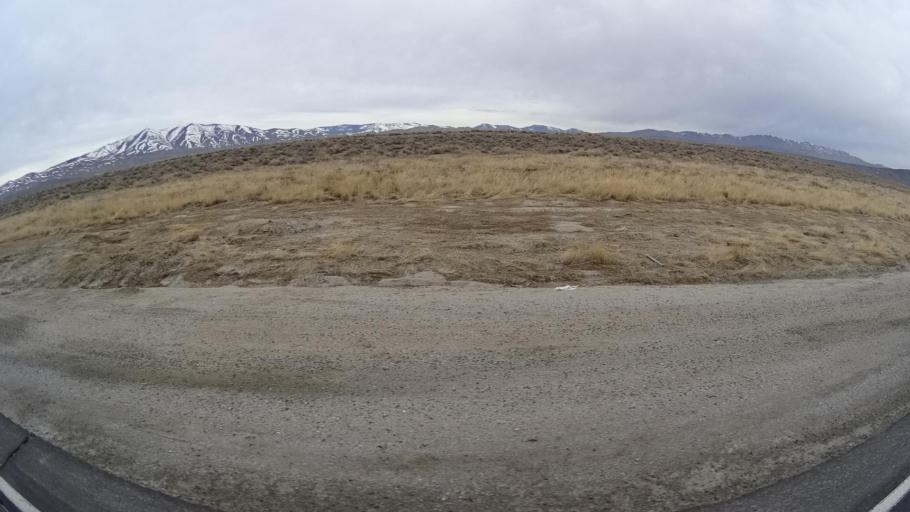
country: US
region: Nevada
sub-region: Washoe County
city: Lemmon Valley
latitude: 39.6545
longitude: -119.8285
